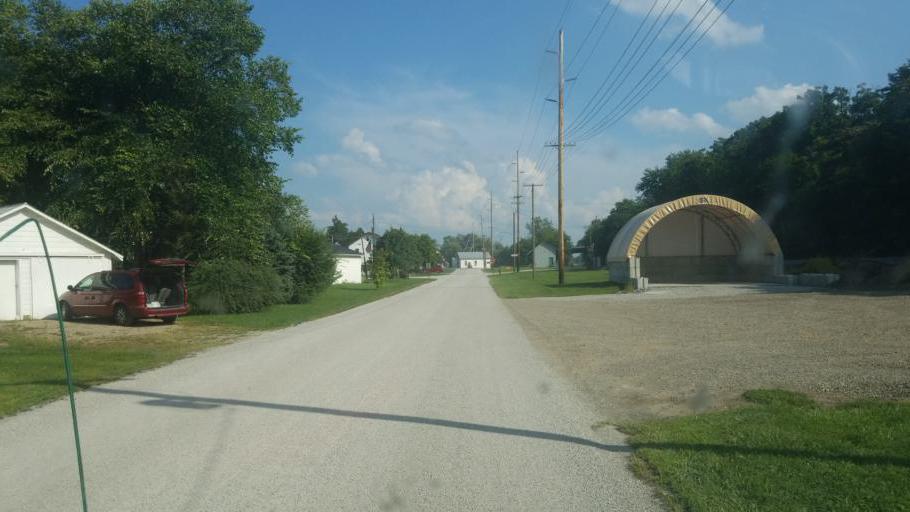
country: US
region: Ohio
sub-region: Medina County
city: Lodi
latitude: 41.0320
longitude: -82.0144
